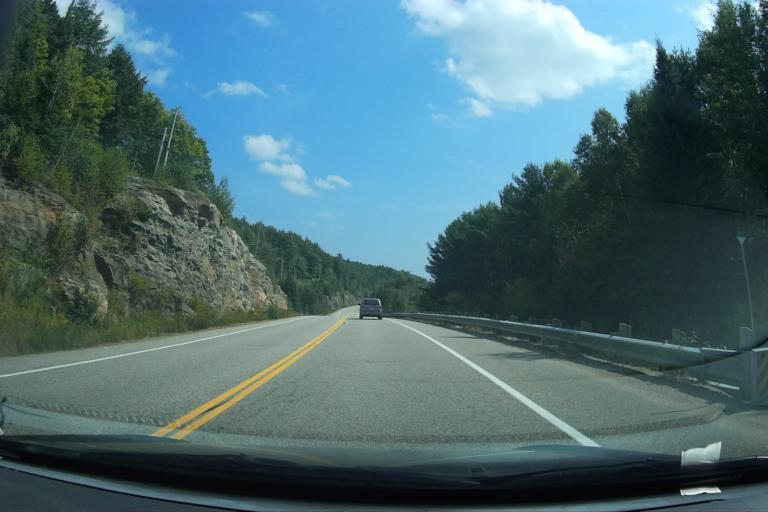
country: CA
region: Ontario
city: Mattawa
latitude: 45.5832
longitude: -78.4730
